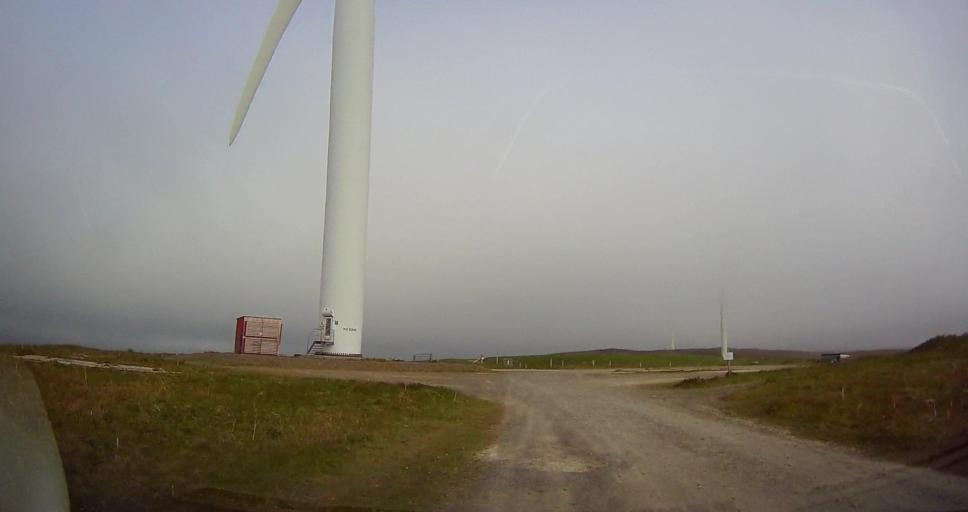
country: GB
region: Scotland
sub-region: Orkney Islands
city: Stromness
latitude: 59.1154
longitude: -3.1466
